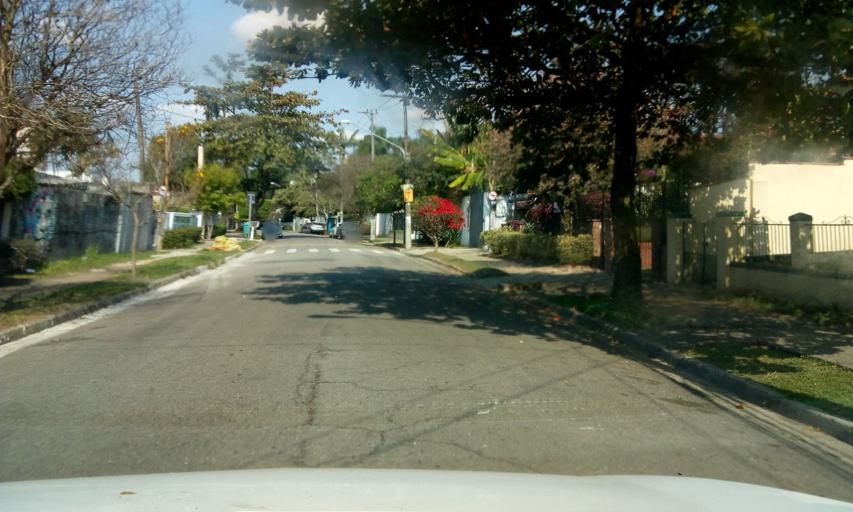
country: BR
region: Sao Paulo
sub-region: Osasco
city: Osasco
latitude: -23.5255
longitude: -46.7172
